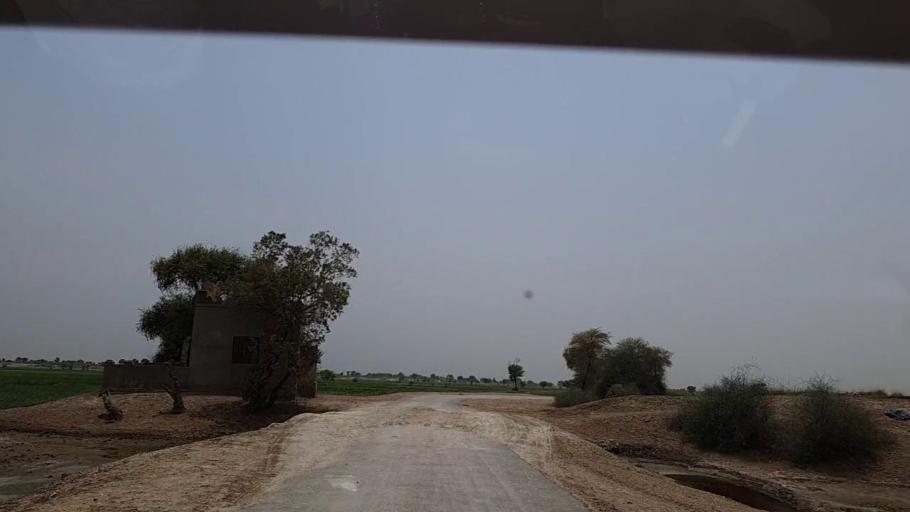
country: PK
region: Sindh
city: Khairpur Nathan Shah
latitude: 27.0069
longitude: 67.6530
